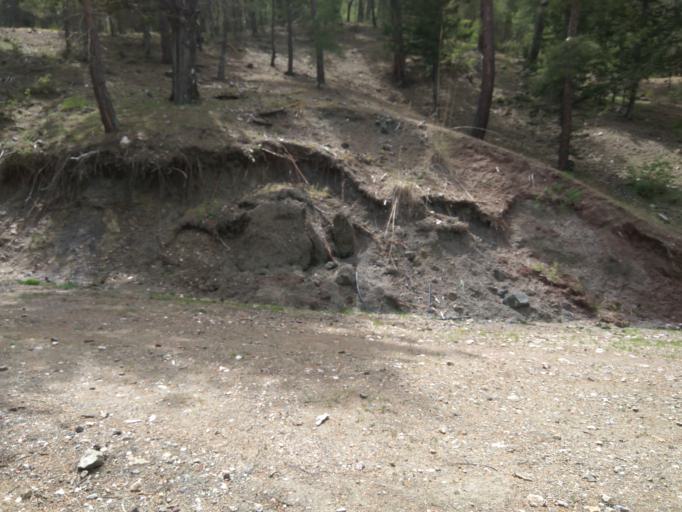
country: TR
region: Antalya
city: Altinyaka
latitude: 36.6019
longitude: 30.4240
